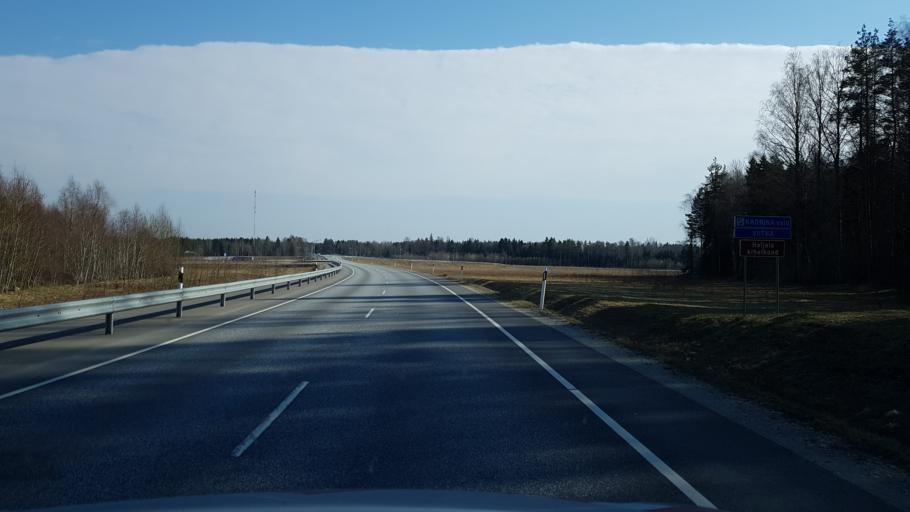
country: EE
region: Laeaene-Virumaa
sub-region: Kadrina vald
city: Kadrina
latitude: 59.4676
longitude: 25.9987
